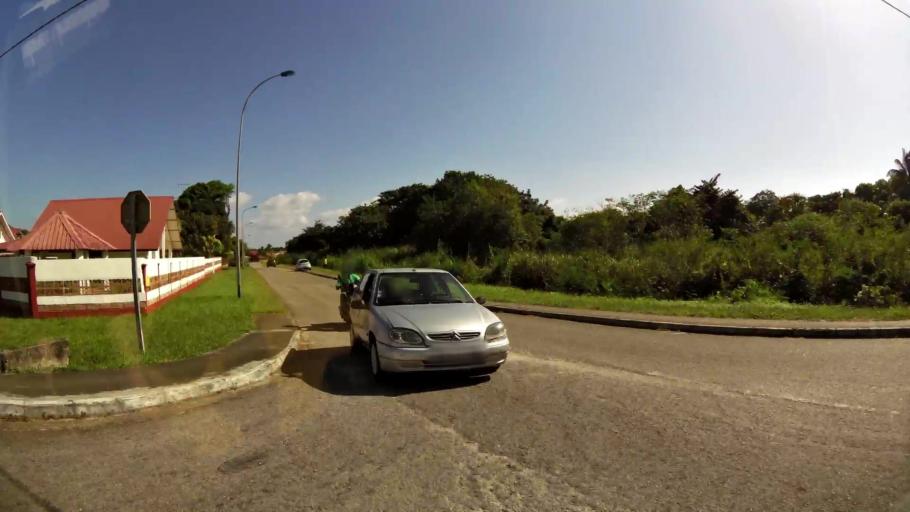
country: GF
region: Guyane
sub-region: Guyane
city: Remire-Montjoly
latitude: 4.9100
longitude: -52.2759
